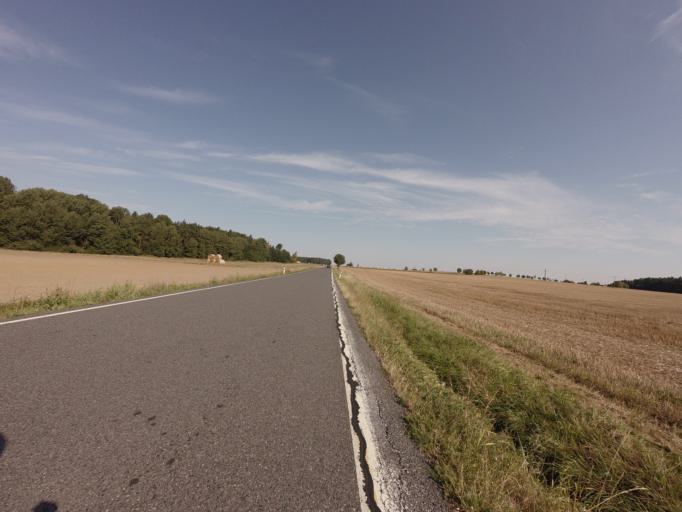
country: CZ
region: Jihocesky
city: Bernartice
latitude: 49.3160
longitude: 14.3721
